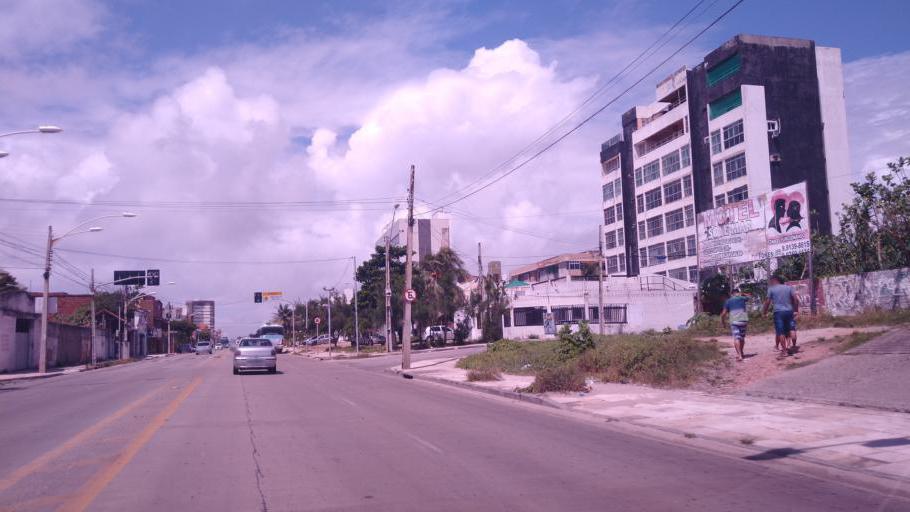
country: BR
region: Ceara
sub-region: Fortaleza
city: Fortaleza
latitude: -3.7252
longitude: -38.4623
